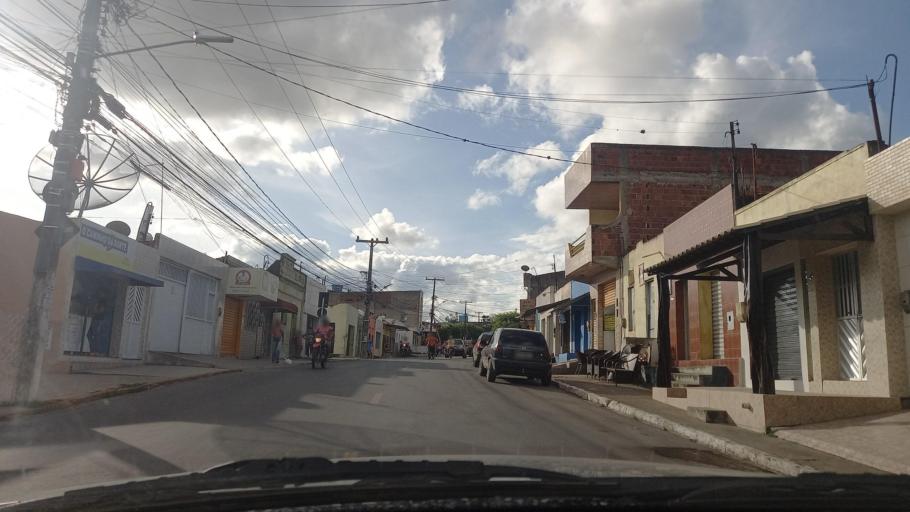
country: BR
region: Pernambuco
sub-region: Gravata
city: Gravata
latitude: -8.1995
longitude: -35.5719
